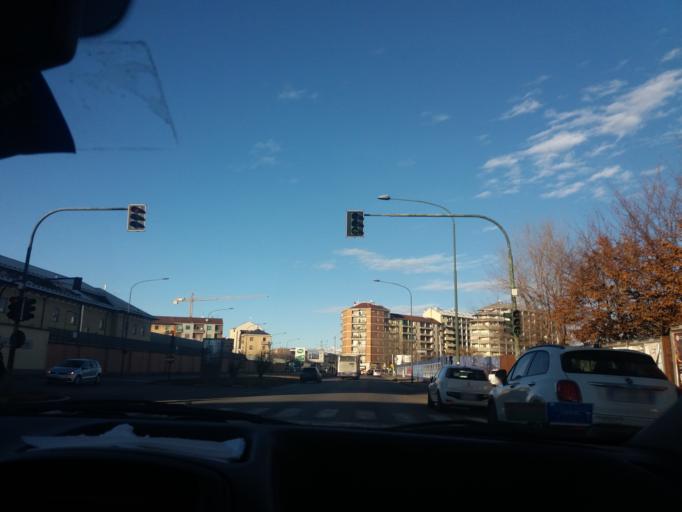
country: IT
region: Piedmont
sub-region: Provincia di Torino
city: Lesna
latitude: 45.0520
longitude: 7.6299
